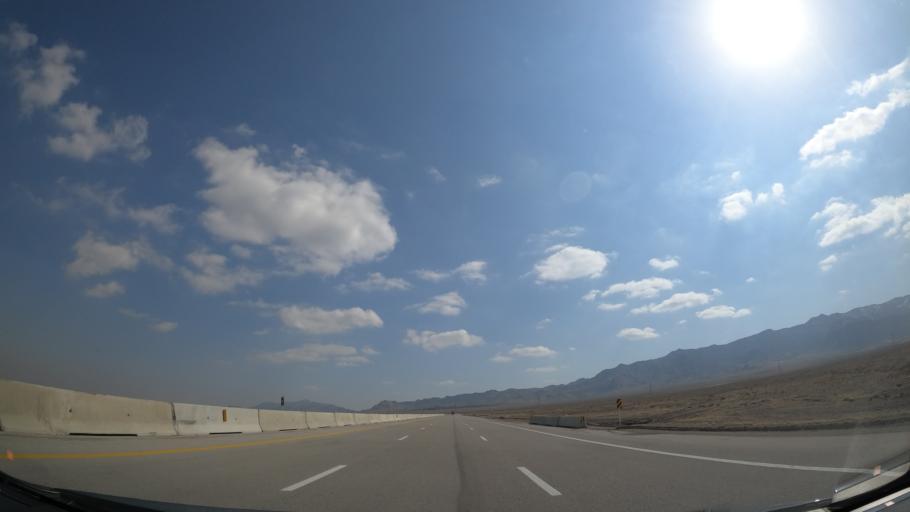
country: IR
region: Alborz
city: Eshtehard
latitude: 35.7222
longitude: 50.5681
